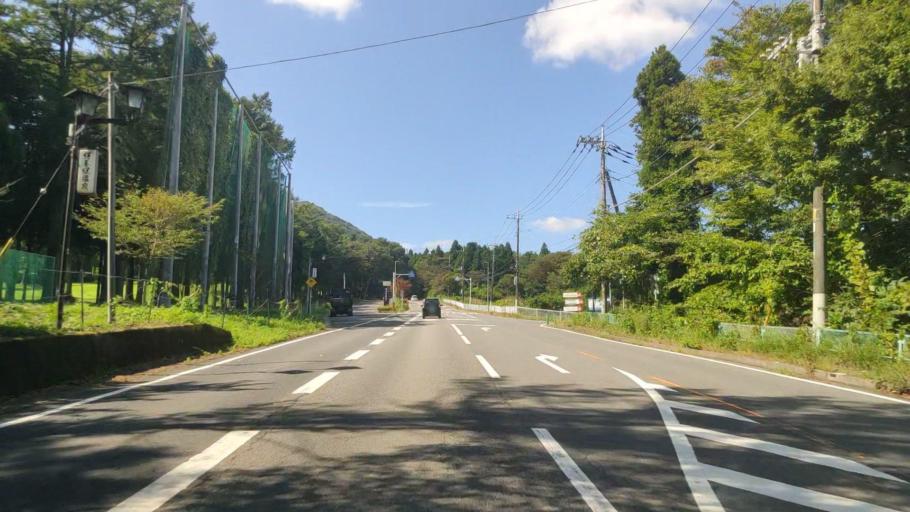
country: JP
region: Gunma
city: Shibukawa
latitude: 36.4988
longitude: 138.9349
